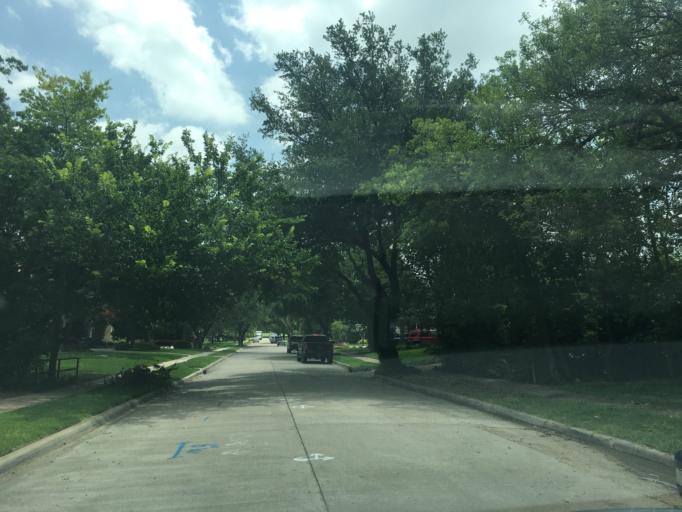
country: US
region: Texas
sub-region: Dallas County
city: University Park
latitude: 32.8725
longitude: -96.7948
